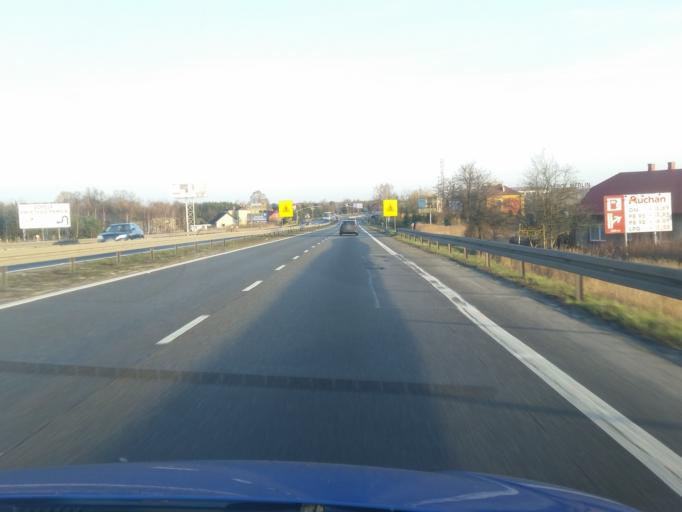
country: PL
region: Silesian Voivodeship
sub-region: Powiat czestochowski
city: Huta Stara B
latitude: 50.7375
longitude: 19.1593
